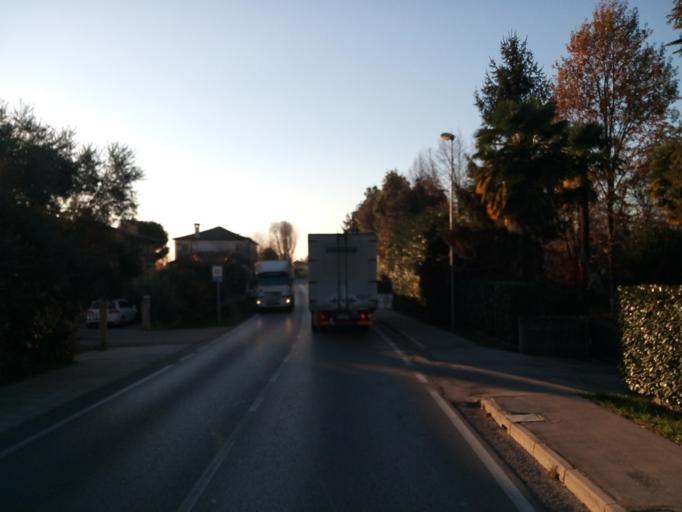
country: IT
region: Veneto
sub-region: Provincia di Vicenza
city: Mussolente
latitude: 45.7788
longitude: 11.8196
